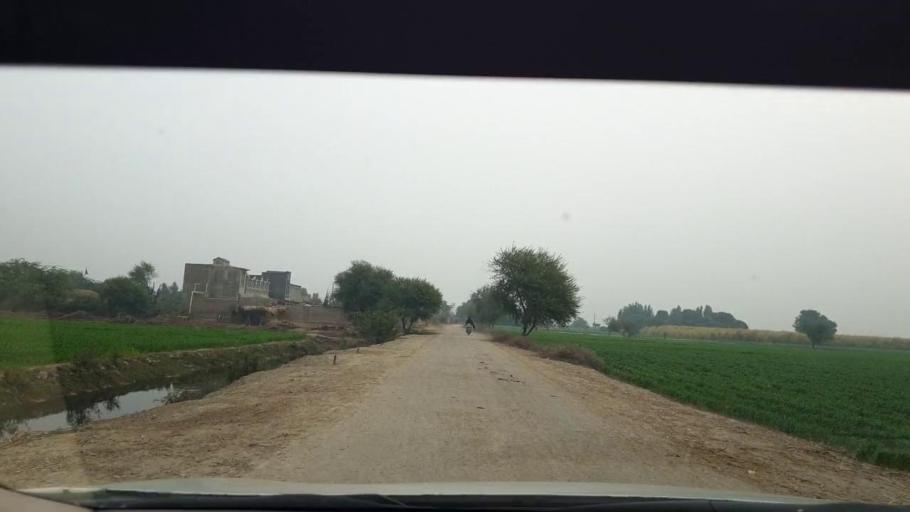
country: PK
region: Sindh
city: Berani
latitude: 25.8752
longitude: 68.8316
